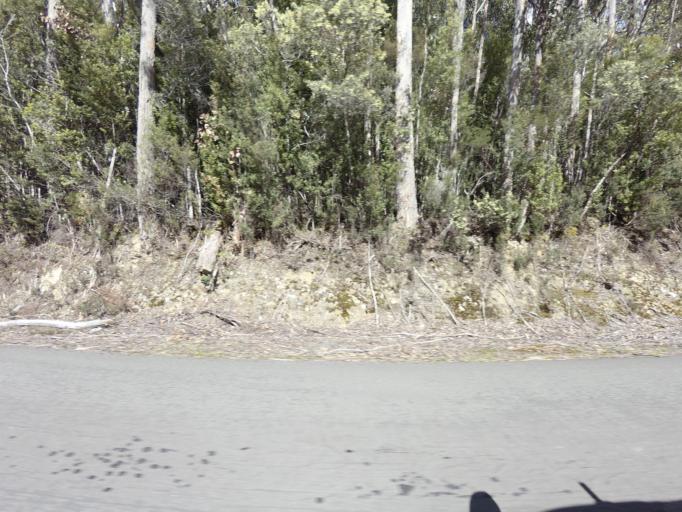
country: AU
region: Tasmania
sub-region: Derwent Valley
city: New Norfolk
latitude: -42.7357
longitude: 146.4877
